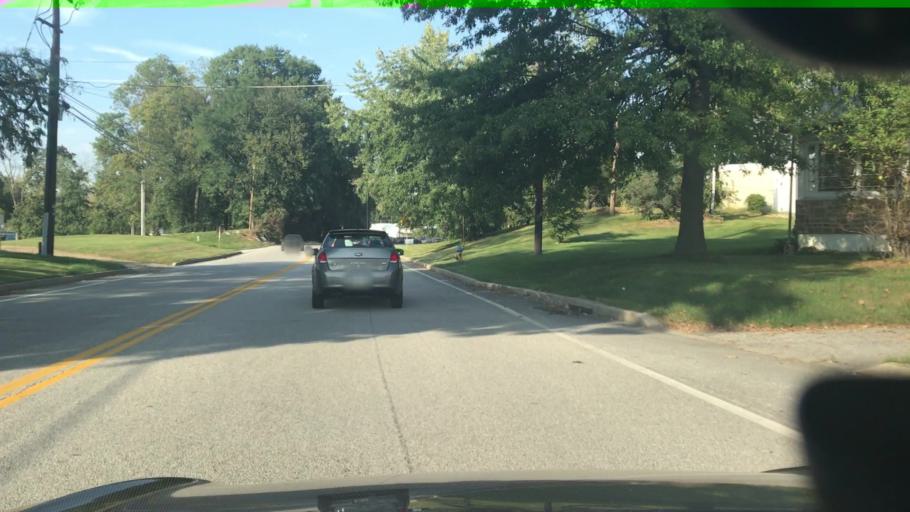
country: US
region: Pennsylvania
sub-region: Cumberland County
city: Shiremanstown
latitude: 40.2150
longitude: -76.9489
